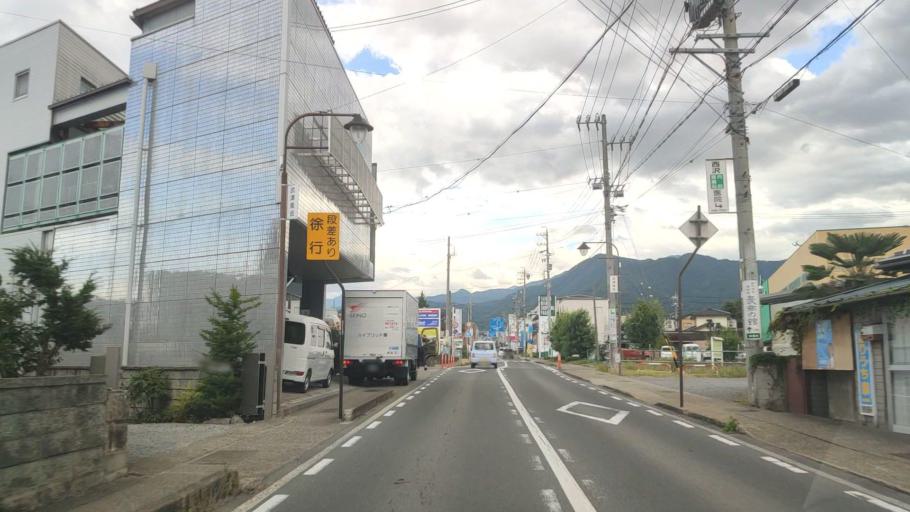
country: JP
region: Nagano
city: Suzaka
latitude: 36.6546
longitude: 138.3020
